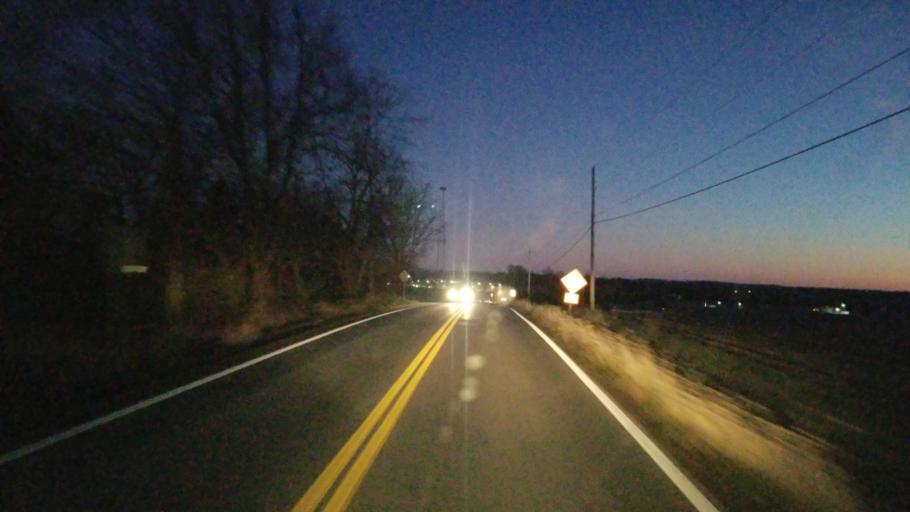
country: US
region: Ohio
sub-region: Highland County
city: Leesburg
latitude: 39.3372
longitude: -83.5508
